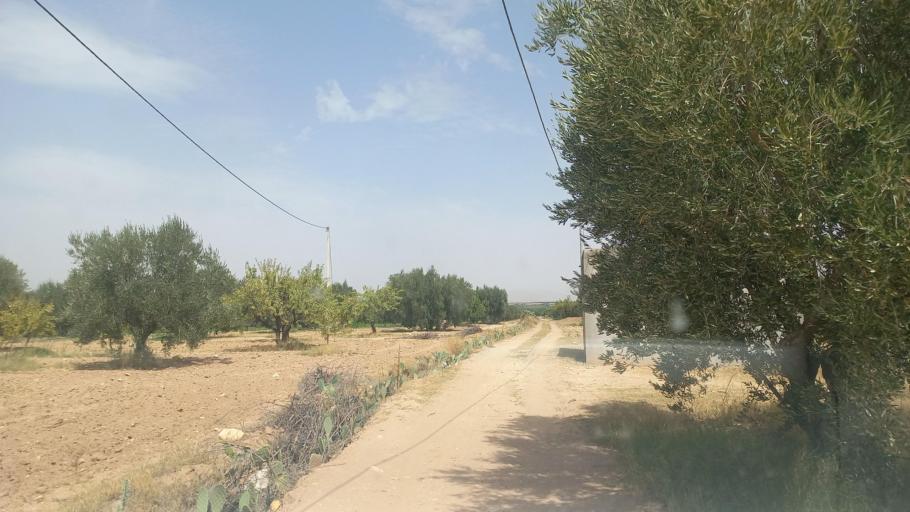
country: TN
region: Al Qasrayn
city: Kasserine
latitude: 35.2619
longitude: 9.0002
